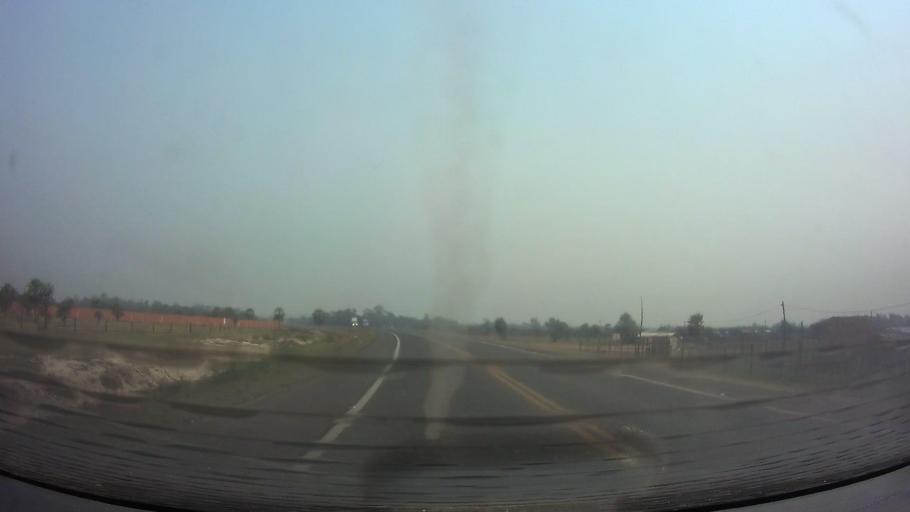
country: PY
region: Central
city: Limpio
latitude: -25.1540
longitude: -57.4859
